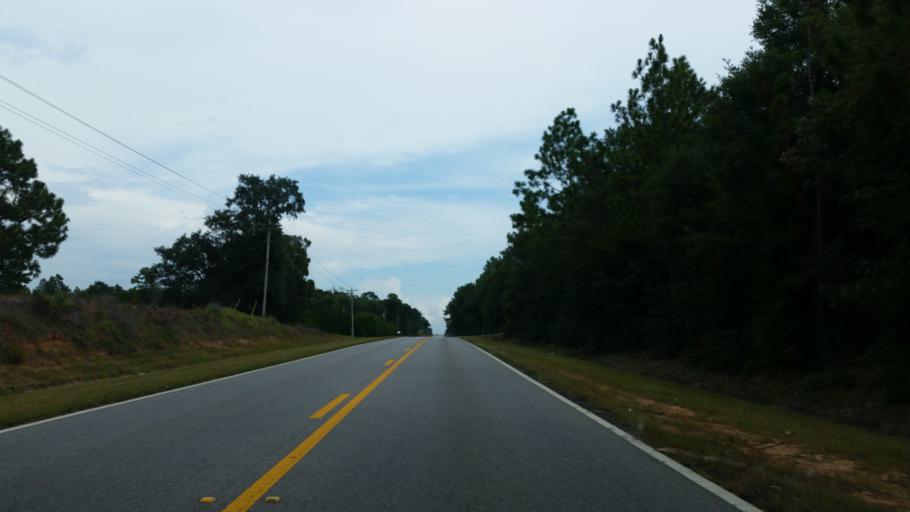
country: US
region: Florida
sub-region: Santa Rosa County
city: Wallace
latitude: 30.6676
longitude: -87.2103
